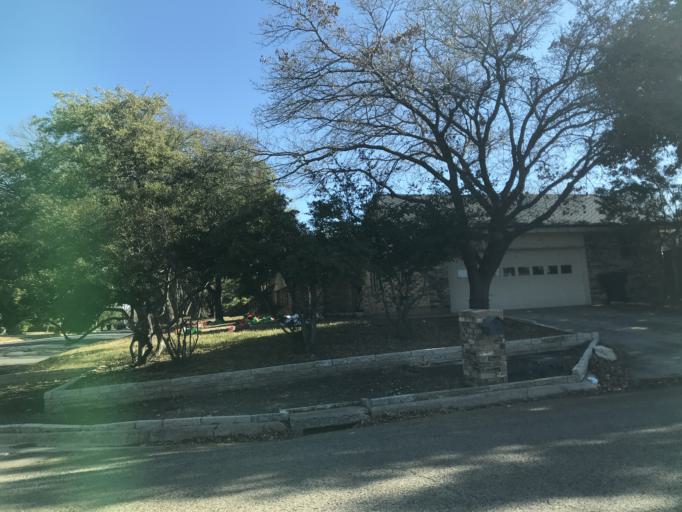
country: US
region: Texas
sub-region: Taylor County
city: Abilene
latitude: 32.3810
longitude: -99.7596
